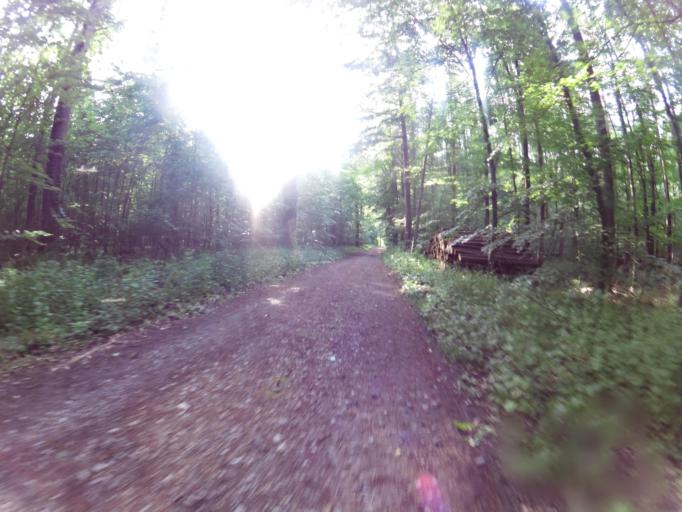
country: DE
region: Bavaria
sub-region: Regierungsbezirk Unterfranken
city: Frickenhausen
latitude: 49.6965
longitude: 10.0749
